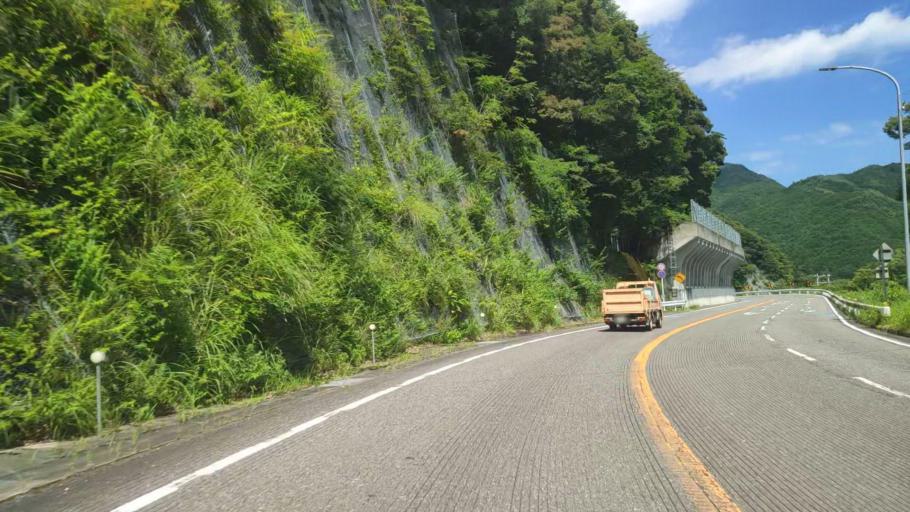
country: JP
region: Mie
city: Owase
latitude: 33.9192
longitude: 136.1039
